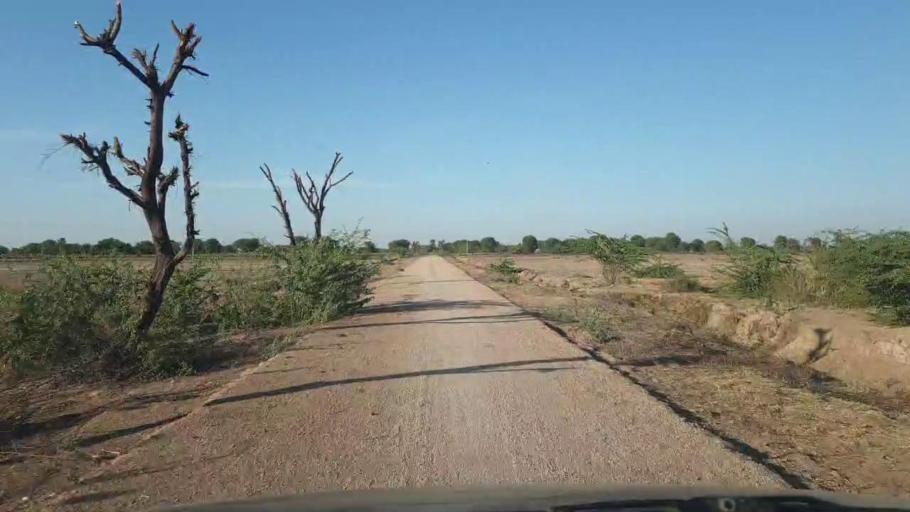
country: PK
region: Sindh
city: Dhoro Naro
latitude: 25.4344
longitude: 69.5364
